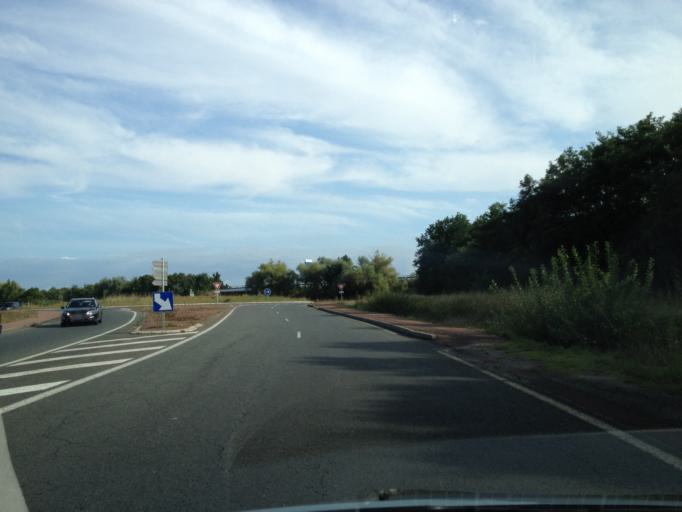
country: FR
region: Poitou-Charentes
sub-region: Departement de la Charente-Maritime
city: Breuil-Magne
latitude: 45.9662
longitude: -0.9802
